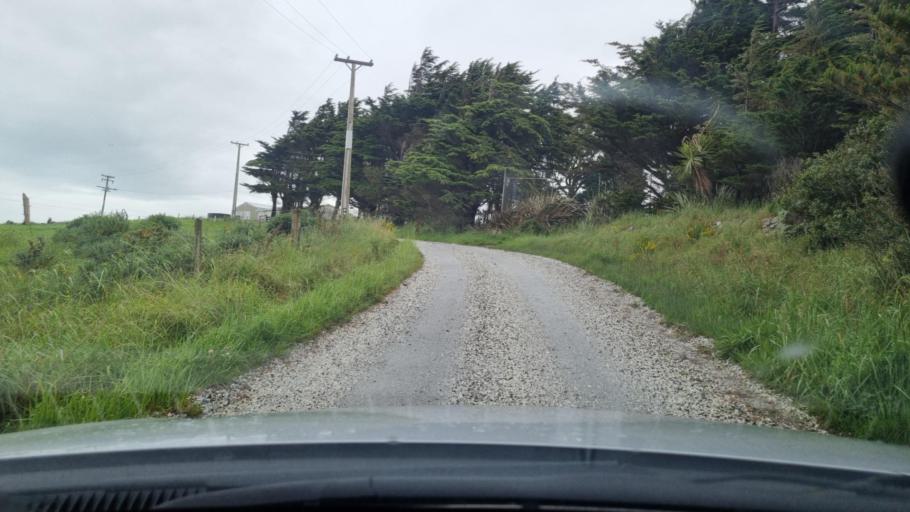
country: NZ
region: Southland
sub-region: Invercargill City
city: Bluff
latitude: -46.5461
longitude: 168.2987
